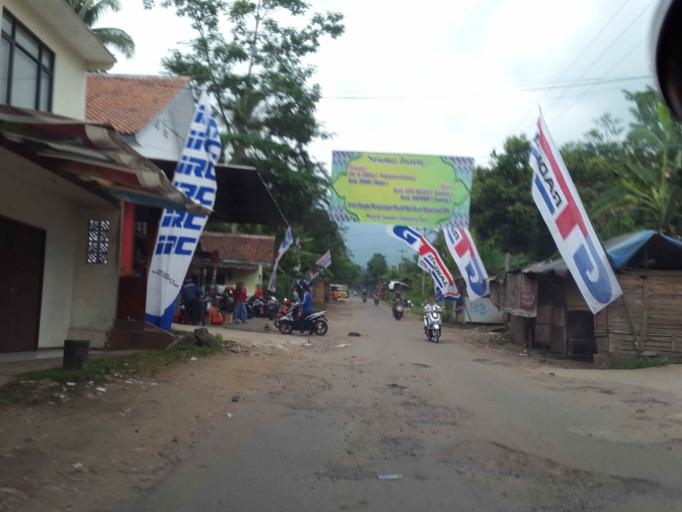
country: ID
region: Banten
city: Majamasjid
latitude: -6.3228
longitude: 106.0905
